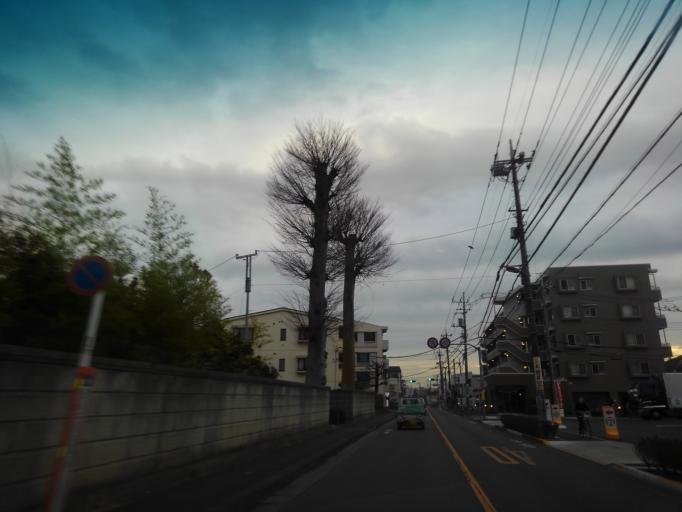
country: JP
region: Tokyo
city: Kokubunji
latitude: 35.7184
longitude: 139.4438
